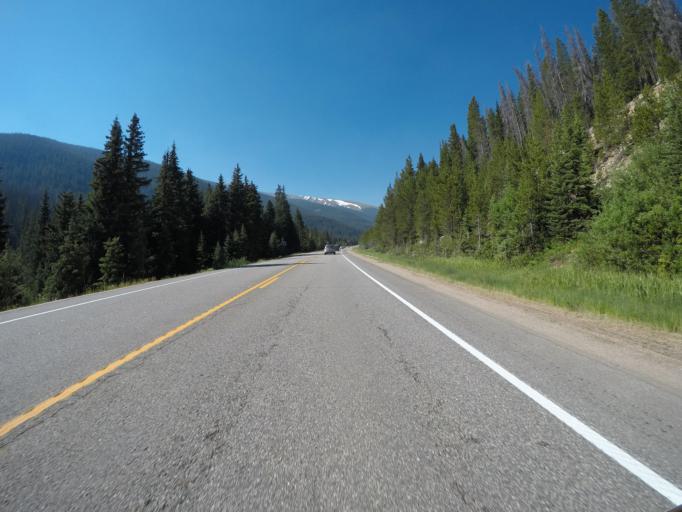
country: US
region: Colorado
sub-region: Grand County
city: Fraser
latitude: 39.8496
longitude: -105.7521
